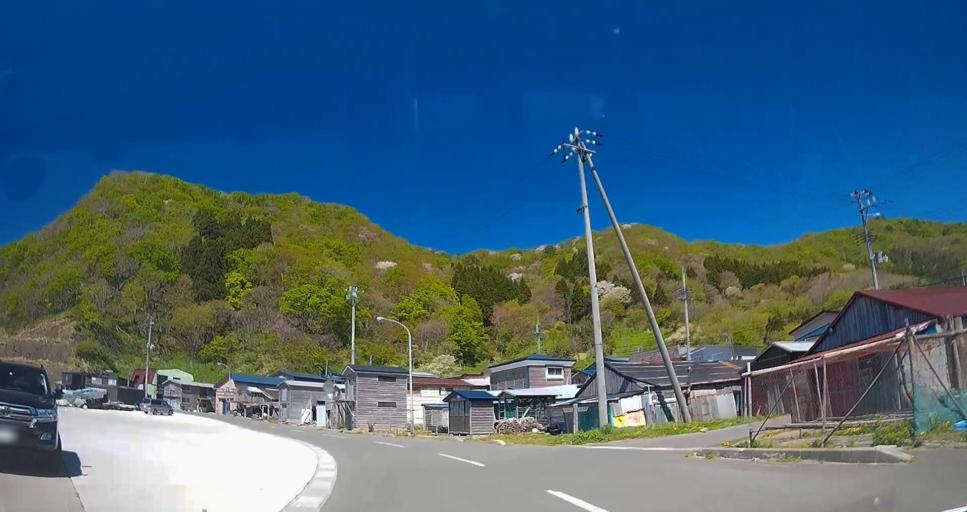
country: JP
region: Aomori
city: Aomori Shi
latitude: 41.1423
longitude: 140.7737
